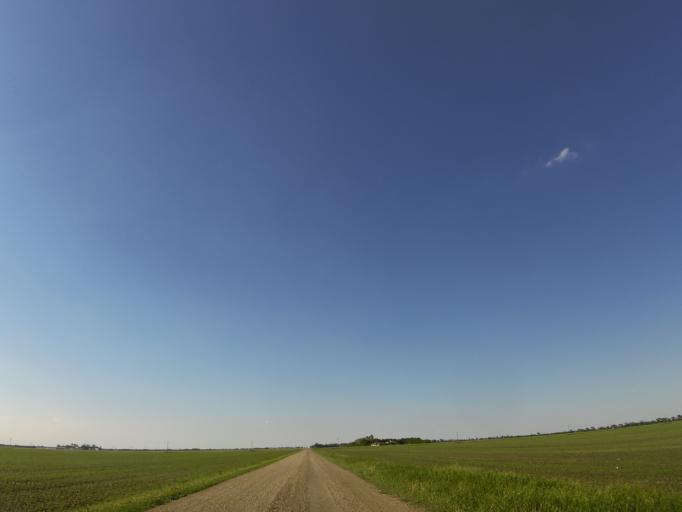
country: US
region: North Dakota
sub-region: Walsh County
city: Grafton
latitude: 48.4065
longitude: -97.2558
